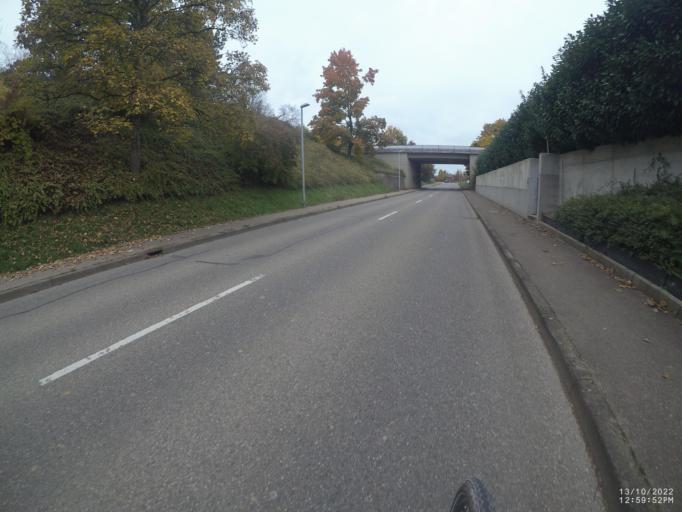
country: DE
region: Baden-Wuerttemberg
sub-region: Regierungsbezirk Stuttgart
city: Schlierbach
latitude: 48.6772
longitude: 9.5201
